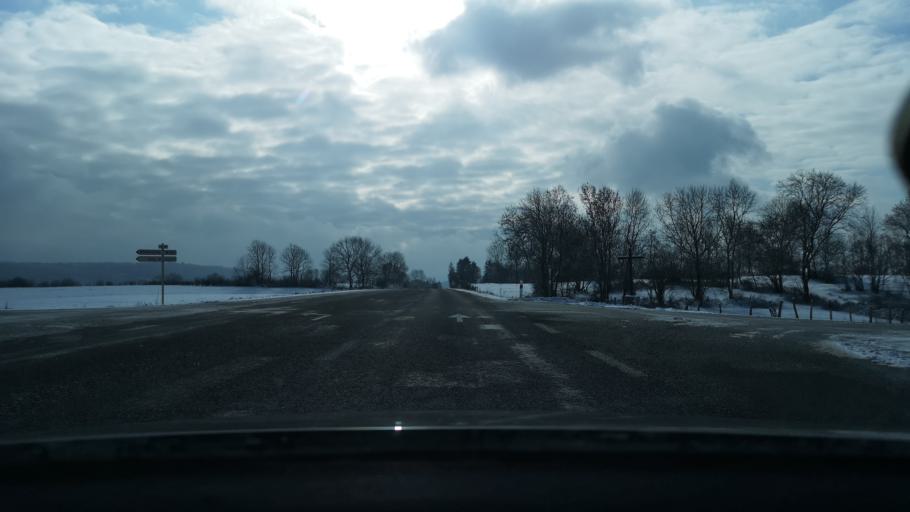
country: FR
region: Franche-Comte
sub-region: Departement du Jura
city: Orgelet
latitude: 46.5591
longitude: 5.5957
